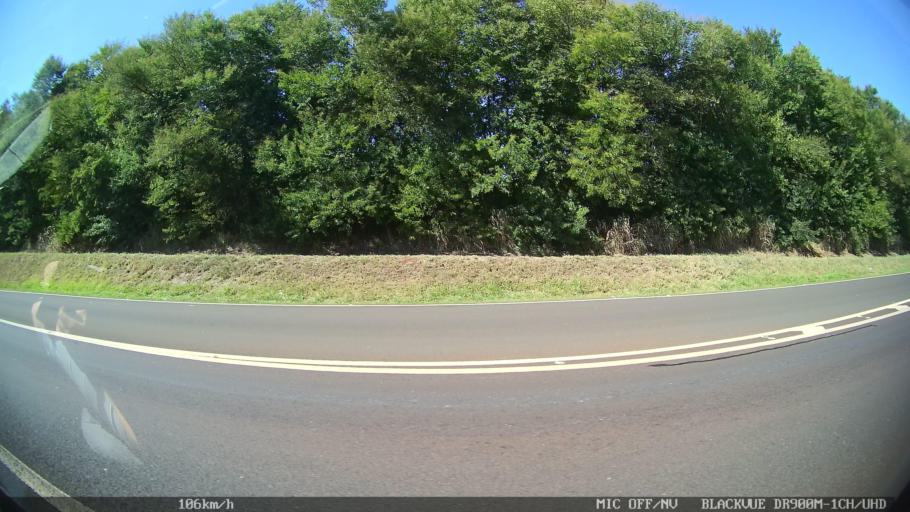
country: BR
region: Sao Paulo
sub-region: Franca
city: Franca
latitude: -20.5890
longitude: -47.4368
